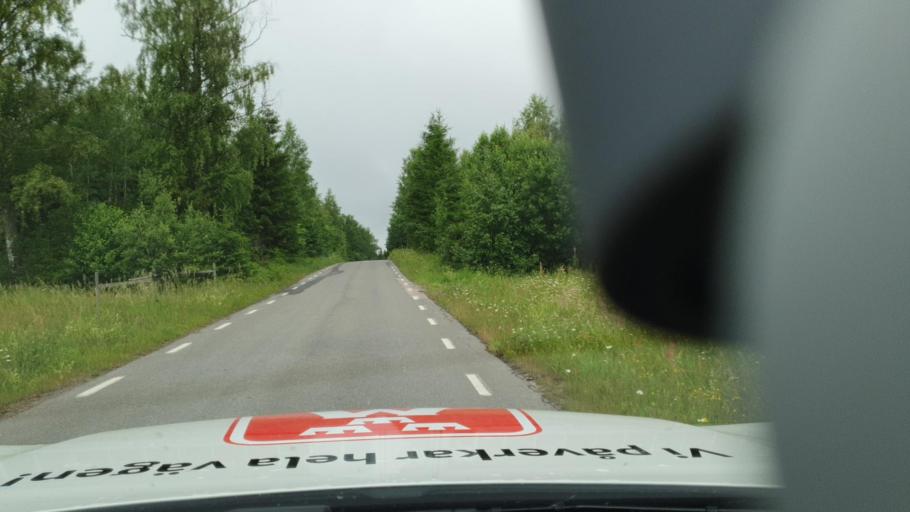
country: SE
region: Vaestra Goetaland
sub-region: Gullspangs Kommun
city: Gullspang
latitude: 59.0301
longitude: 14.1750
